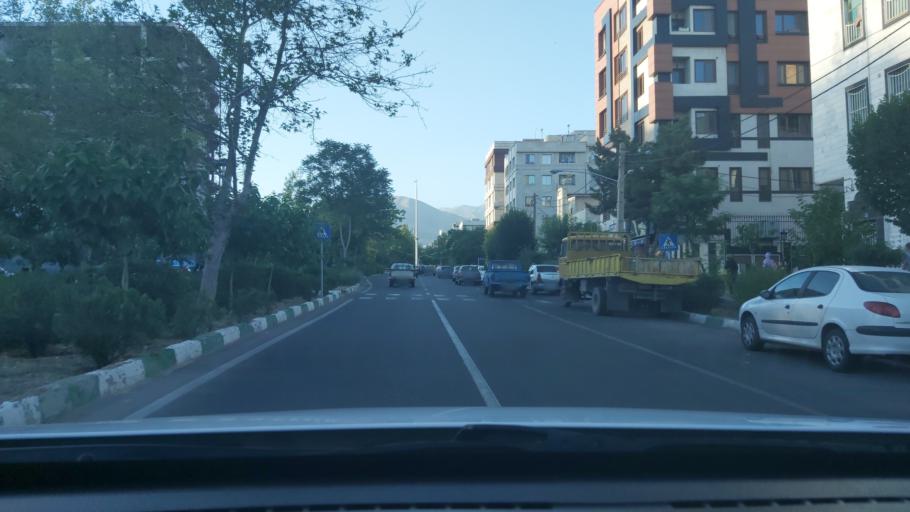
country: IR
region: Tehran
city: Tehran
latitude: 35.7307
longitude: 51.3050
